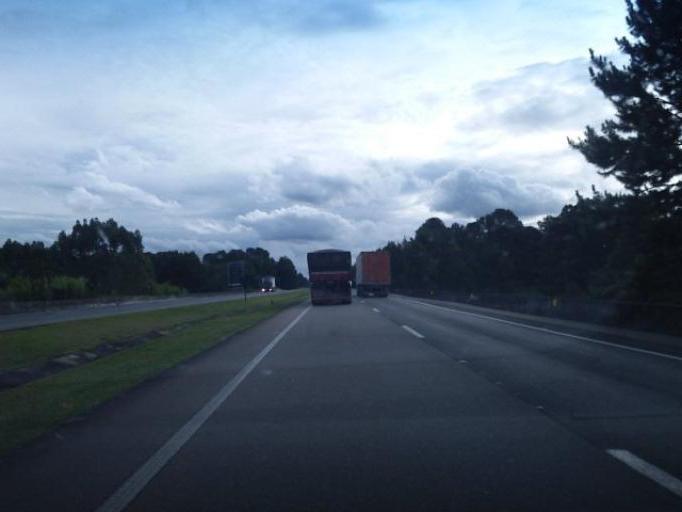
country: BR
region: Parana
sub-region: Piraquara
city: Piraquara
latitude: -25.4099
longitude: -49.0634
